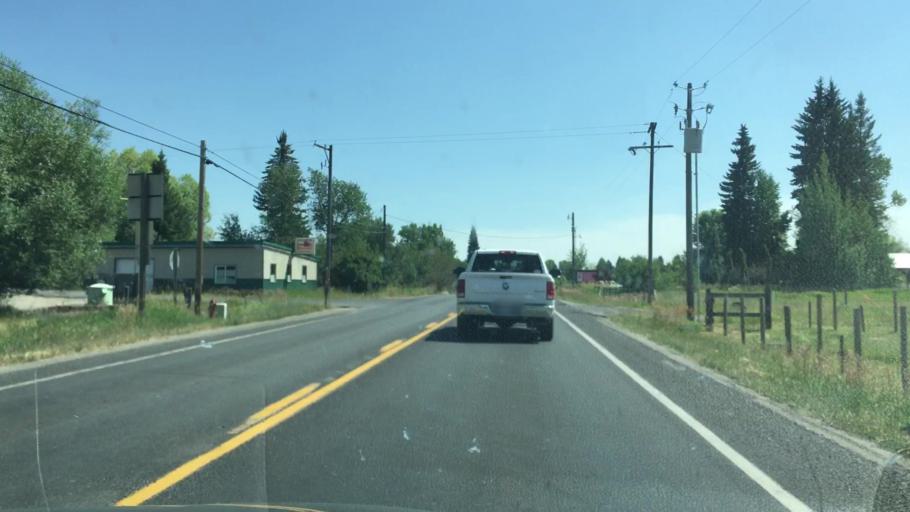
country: US
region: Idaho
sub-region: Valley County
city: McCall
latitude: 44.8910
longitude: -116.0936
